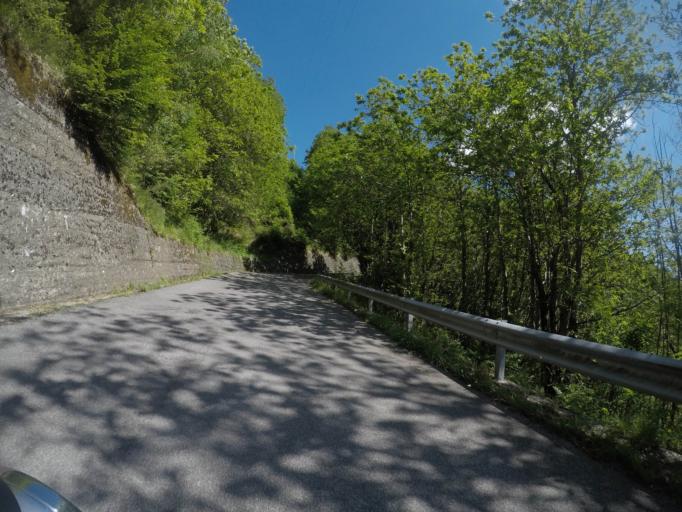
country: IT
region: Tuscany
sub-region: Provincia di Lucca
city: Fontana delle Monache
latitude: 44.0637
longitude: 10.3086
